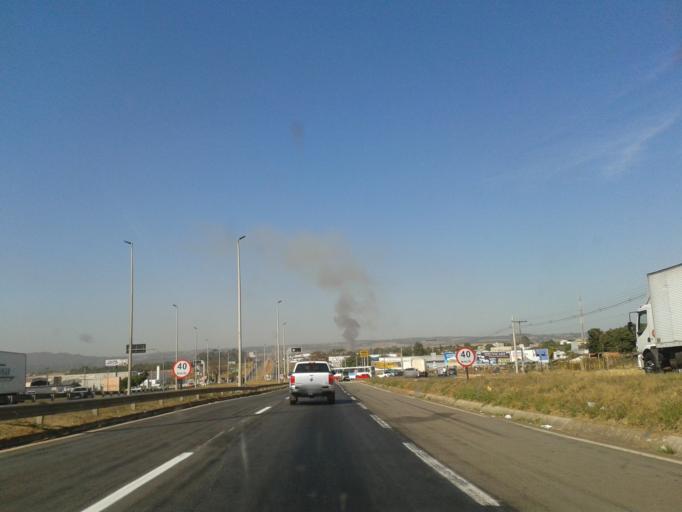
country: BR
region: Goias
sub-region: Aparecida De Goiania
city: Aparecida de Goiania
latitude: -16.8253
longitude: -49.2423
